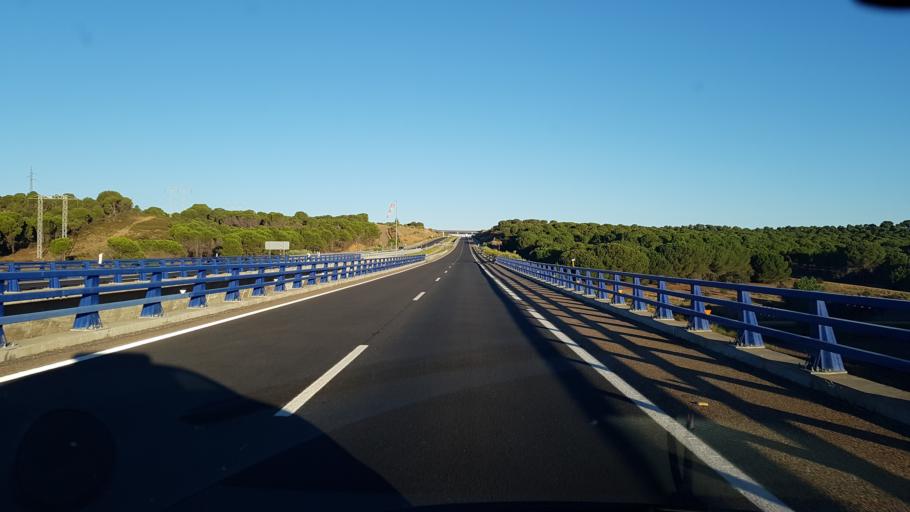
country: ES
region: Castille and Leon
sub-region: Provincia de Zamora
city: Pozoantiguo
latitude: 41.5482
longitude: -5.4410
